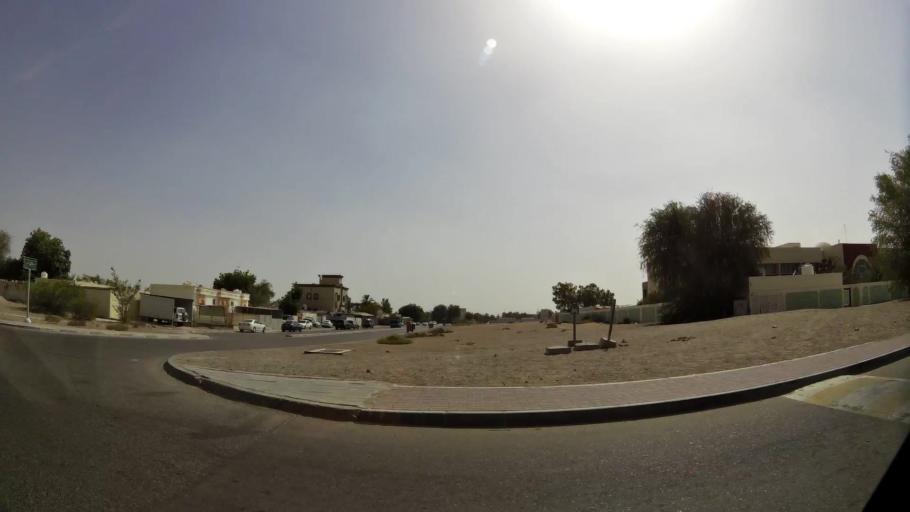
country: AE
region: Abu Dhabi
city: Al Ain
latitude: 24.2341
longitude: 55.6966
